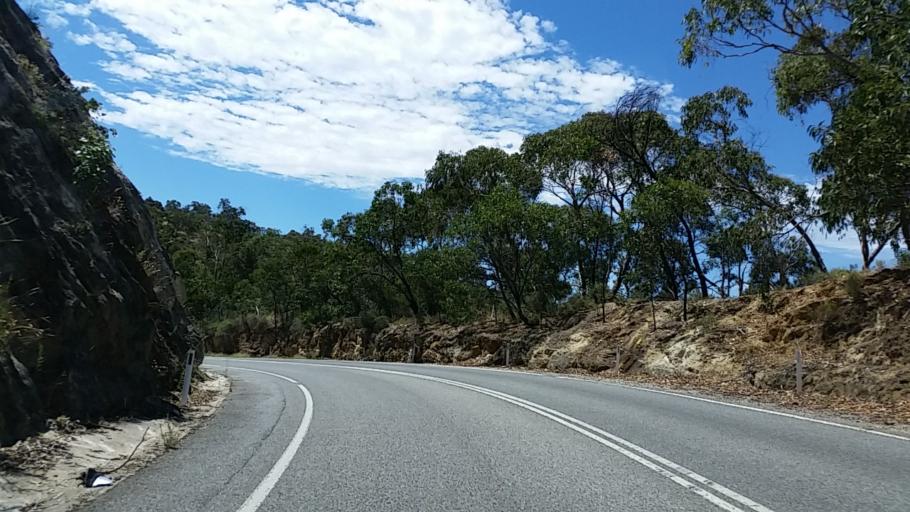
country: AU
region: South Australia
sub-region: Campbelltown
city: Athelstone
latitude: -34.8638
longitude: 138.7842
